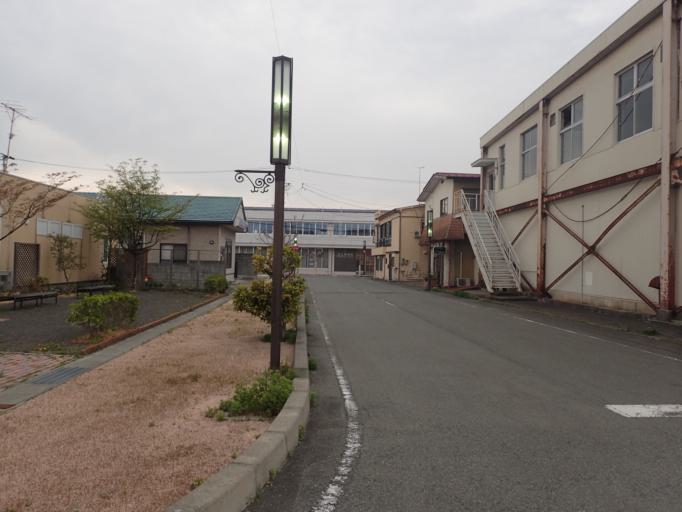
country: JP
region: Fukushima
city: Namie
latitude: 37.4922
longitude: 140.9927
